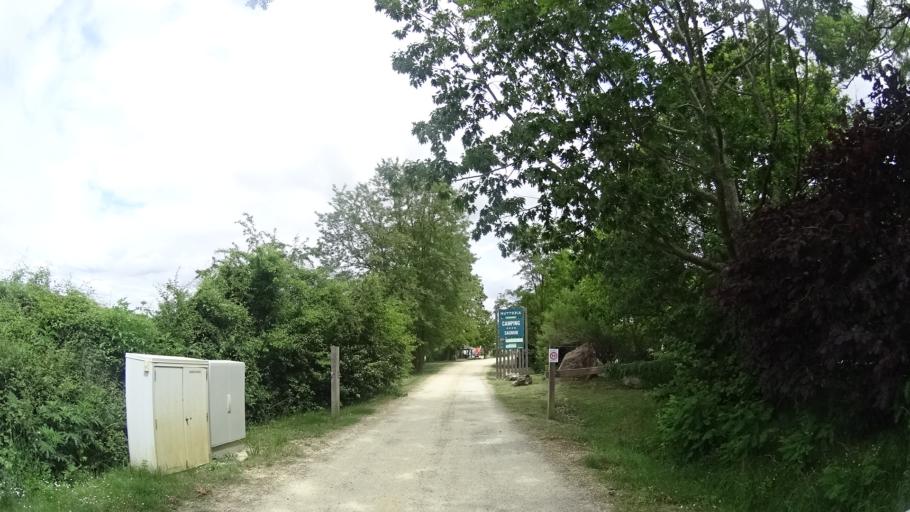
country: FR
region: Pays de la Loire
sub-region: Departement de Maine-et-Loire
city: Chenehutte-Treves-Cunault
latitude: 47.2932
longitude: -0.1435
